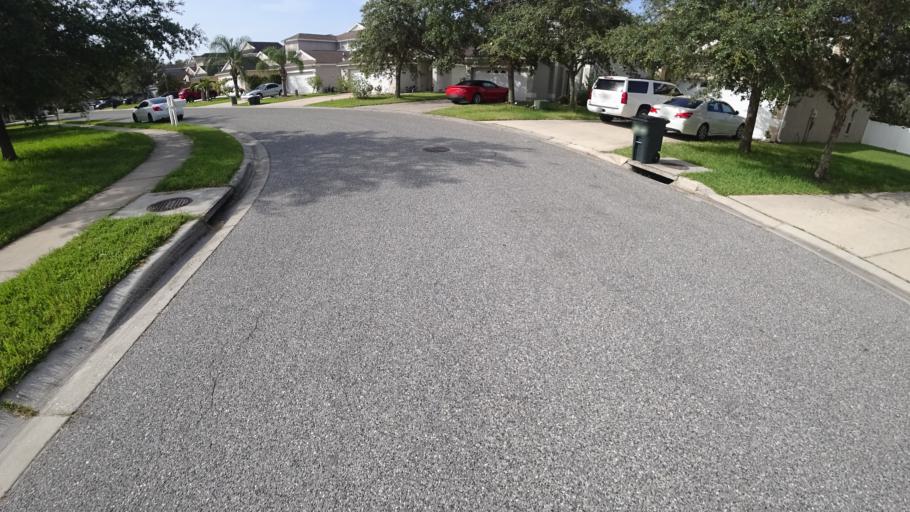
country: US
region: Florida
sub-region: Manatee County
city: Ellenton
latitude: 27.5502
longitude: -82.4965
